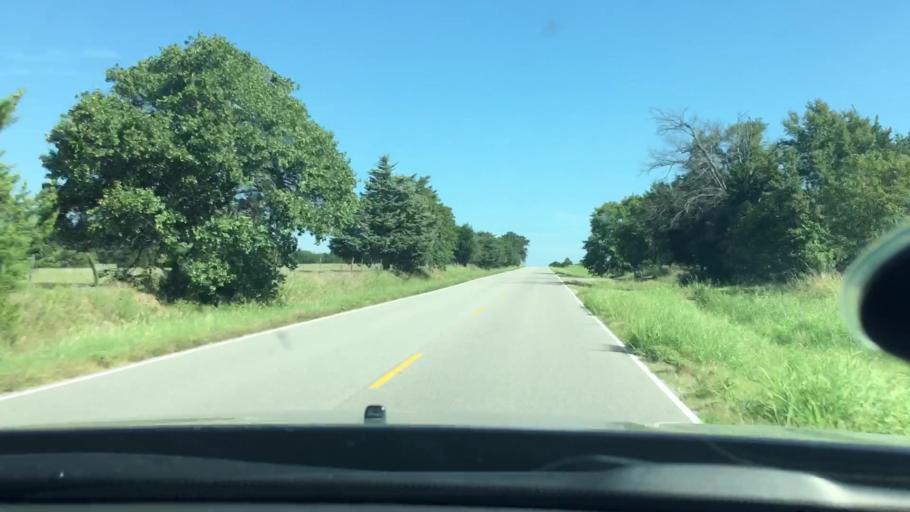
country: US
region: Oklahoma
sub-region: Johnston County
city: Tishomingo
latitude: 34.2955
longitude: -96.5486
